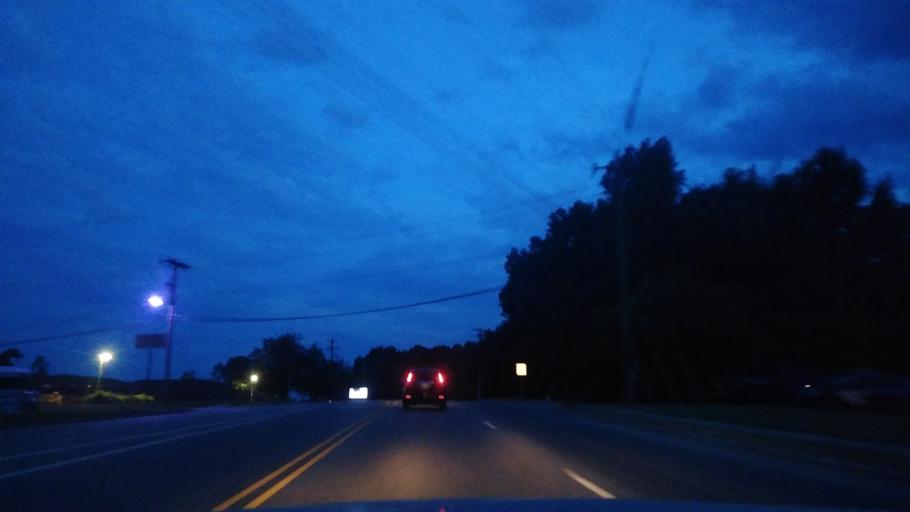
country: US
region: North Carolina
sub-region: Guilford County
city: Jamestown
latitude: 36.0694
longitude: -79.9103
